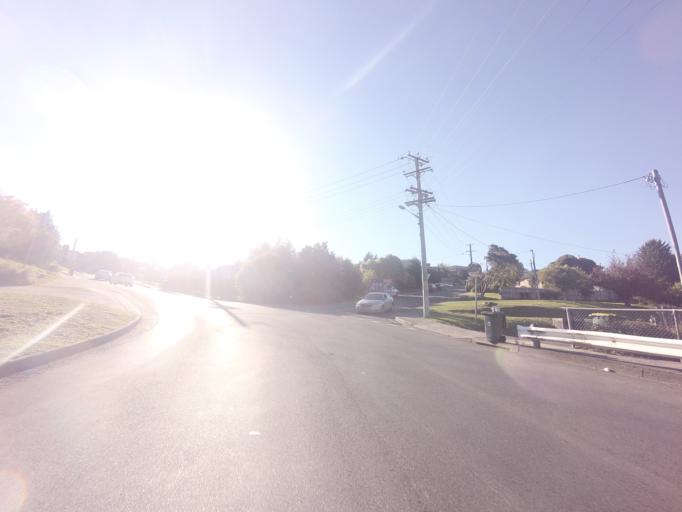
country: AU
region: Tasmania
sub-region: Glenorchy
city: West Moonah
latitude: -42.8625
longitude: 147.2819
